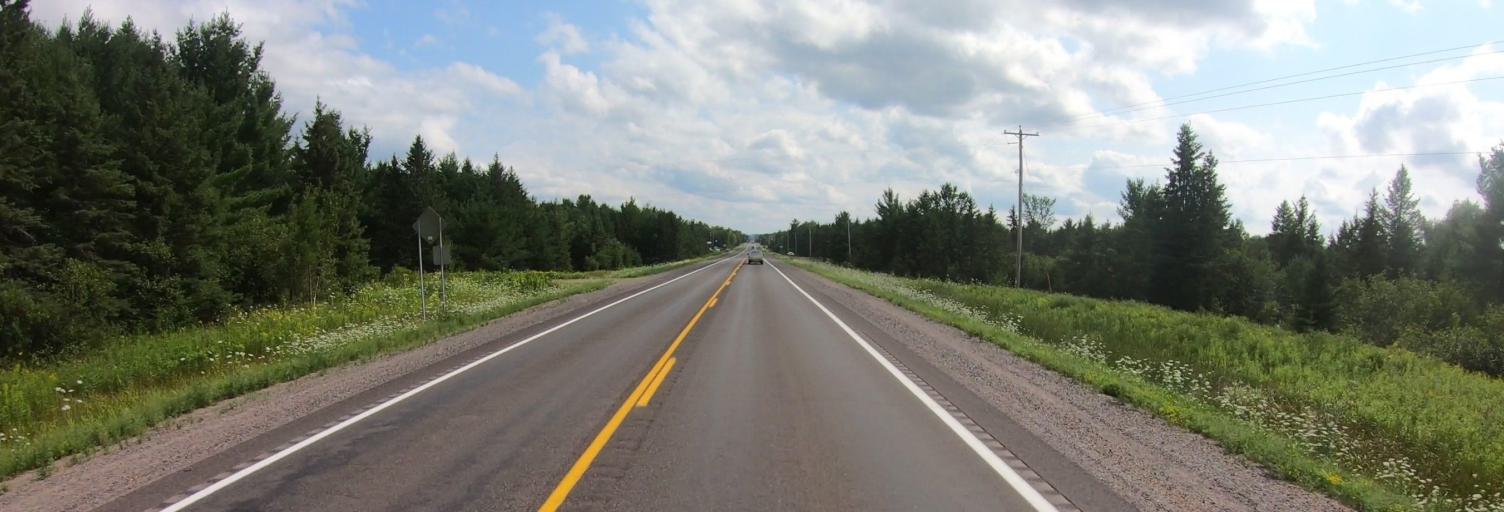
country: US
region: Michigan
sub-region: Ontonagon County
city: Ontonagon
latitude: 46.5528
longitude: -89.1786
